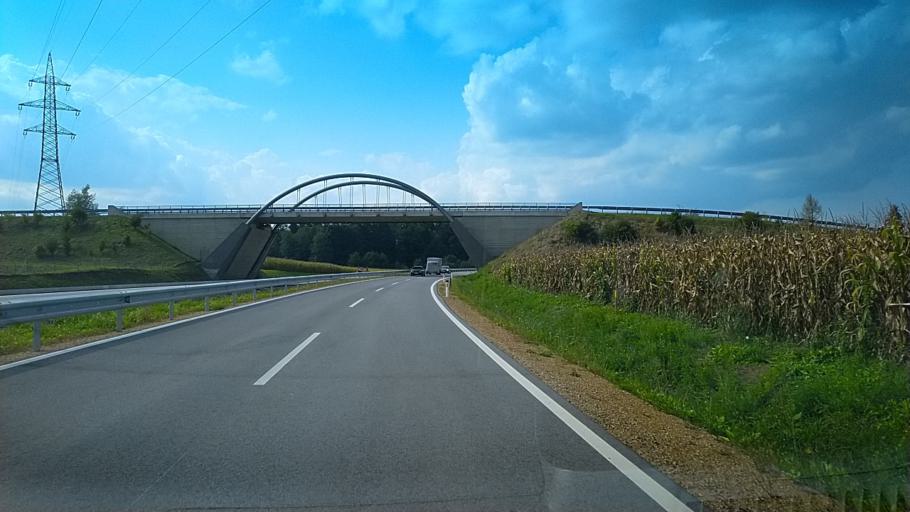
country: AT
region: Styria
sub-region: Politischer Bezirk Deutschlandsberg
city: Gross Sankt Florian
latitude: 46.8146
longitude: 15.2890
